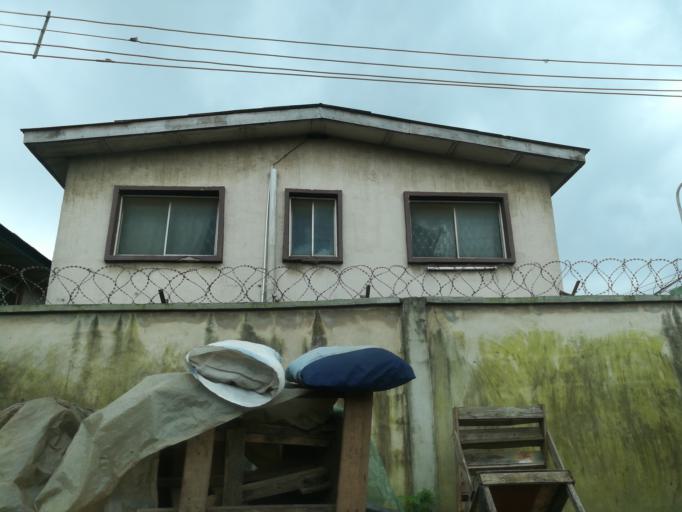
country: NG
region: Lagos
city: Oshodi
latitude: 6.5522
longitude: 3.3392
